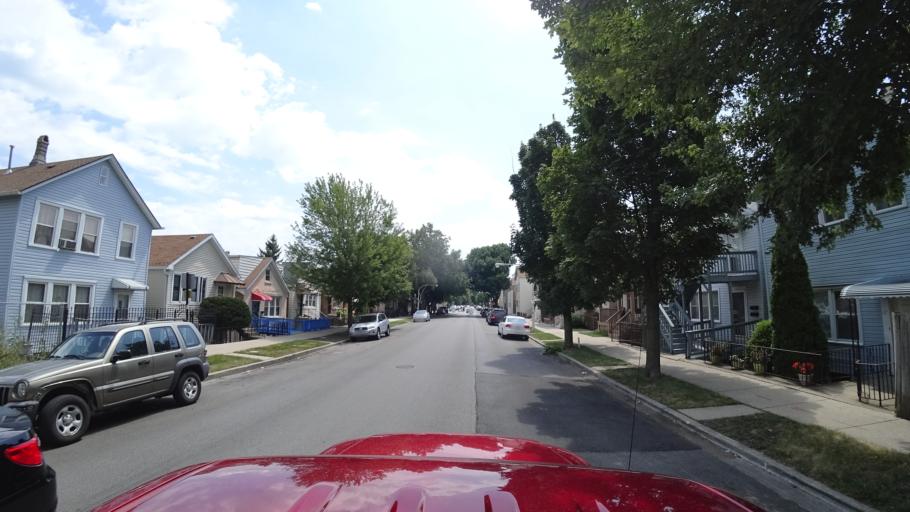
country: US
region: Illinois
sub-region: Cook County
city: Chicago
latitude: 41.8413
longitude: -87.6523
